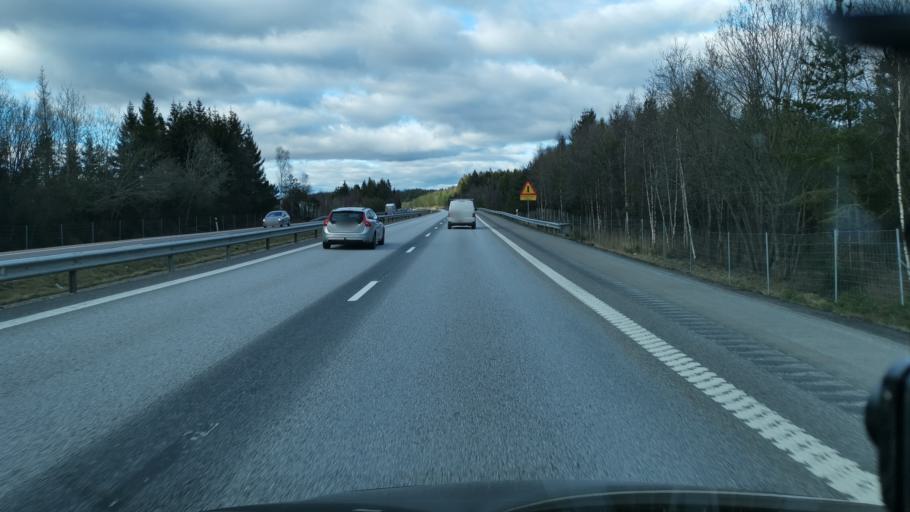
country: SE
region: Vaestra Goetaland
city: Svanesund
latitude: 58.1239
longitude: 11.8828
